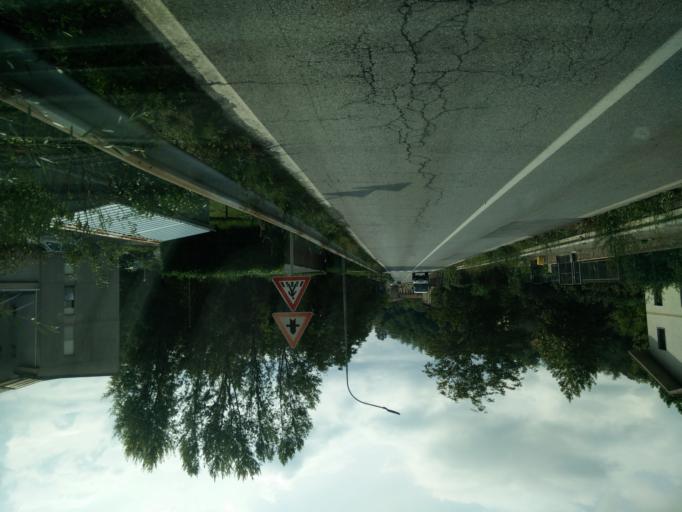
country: IT
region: Tuscany
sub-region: Provincia di Massa-Carrara
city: Filattiera
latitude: 44.3289
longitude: 9.9361
